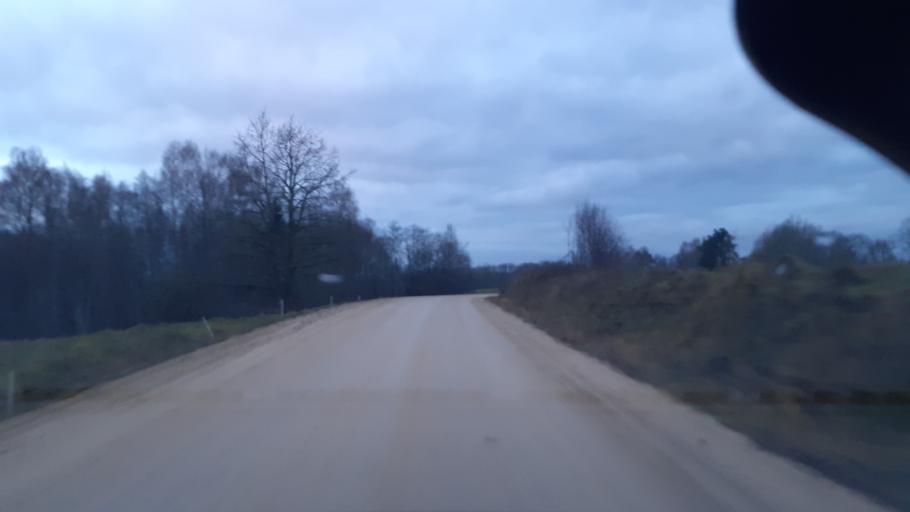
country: LV
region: Kuldigas Rajons
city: Kuldiga
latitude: 56.9576
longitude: 21.8056
